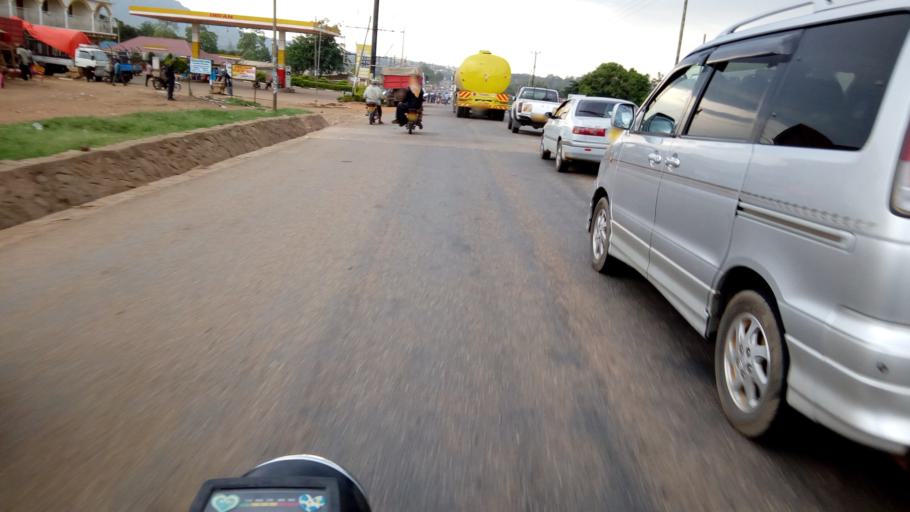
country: UG
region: Eastern Region
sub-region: Mbale District
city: Mbale
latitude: 1.0978
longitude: 34.1754
